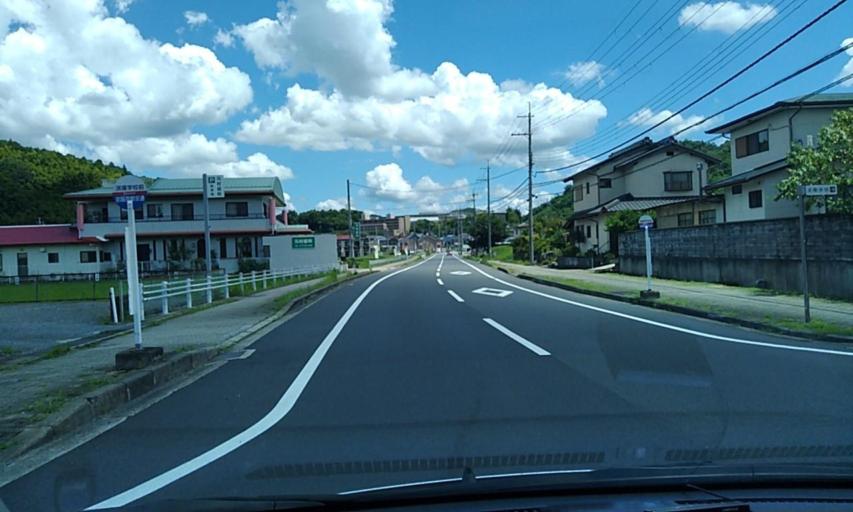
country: JP
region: Kyoto
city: Kameoka
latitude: 35.1004
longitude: 135.4709
